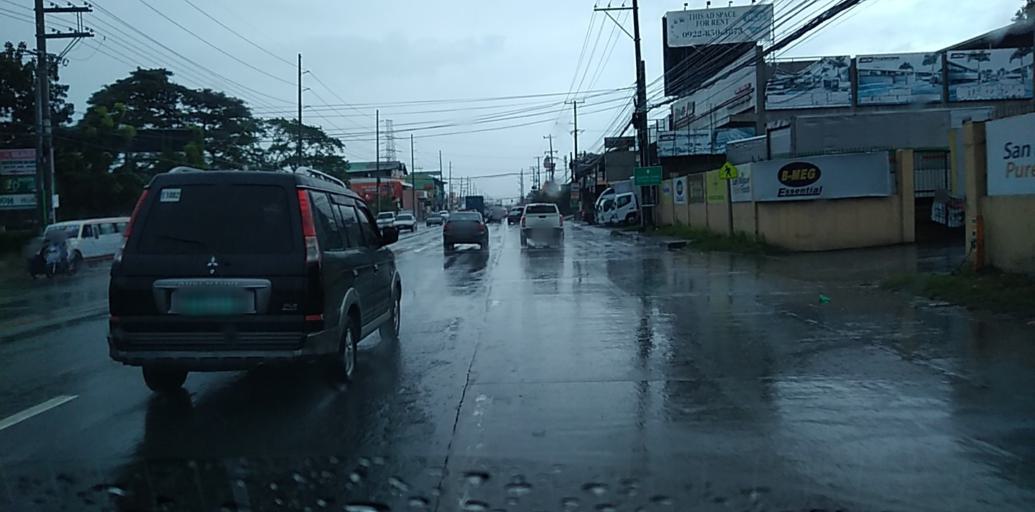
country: PH
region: Central Luzon
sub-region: Province of Pampanga
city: Magliman
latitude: 15.0471
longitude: 120.6691
